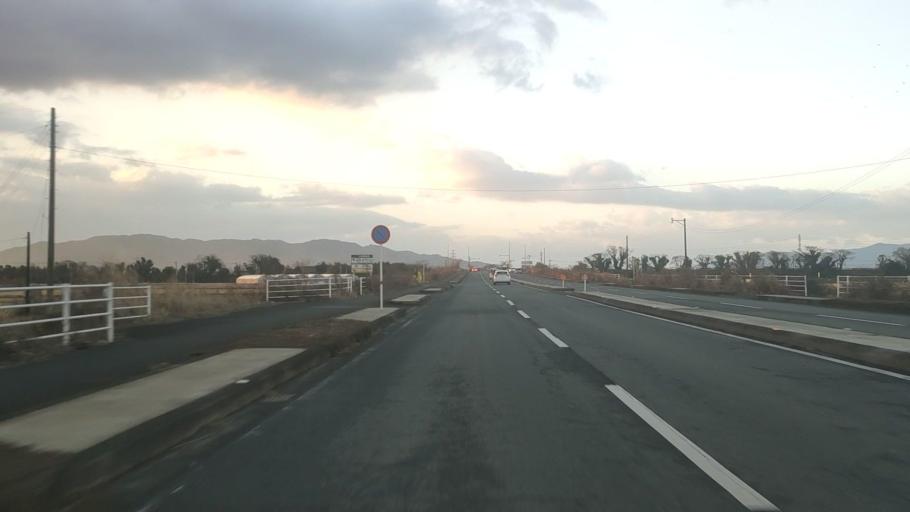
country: JP
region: Kumamoto
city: Kumamoto
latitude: 32.7456
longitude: 130.7063
